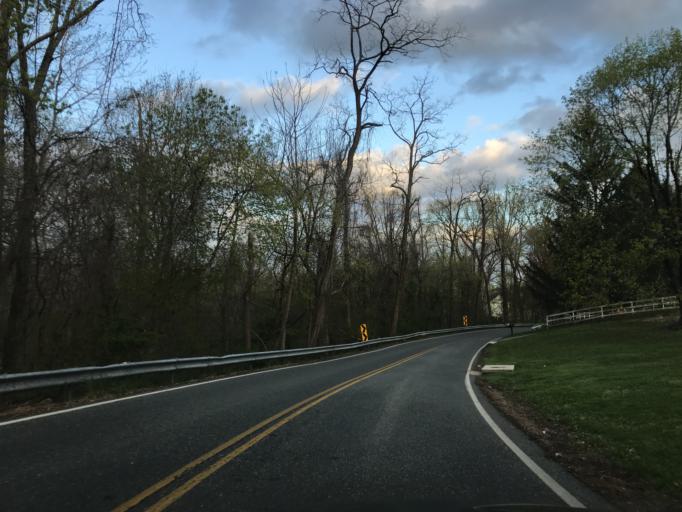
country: US
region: Maryland
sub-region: Harford County
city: South Bel Air
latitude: 39.5319
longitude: -76.3217
